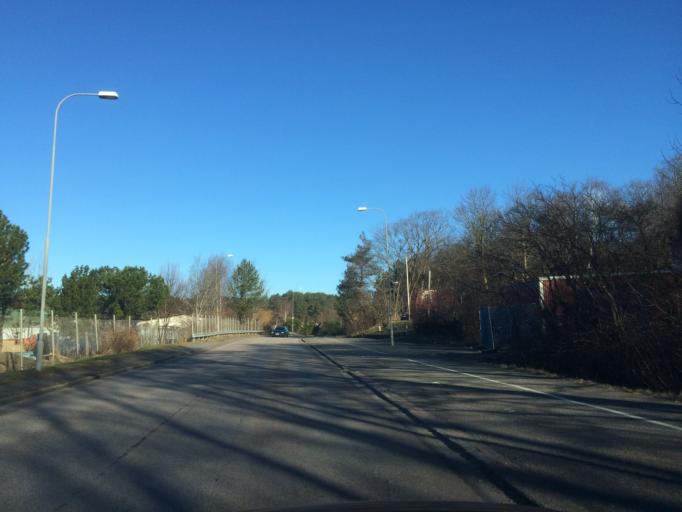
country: SE
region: Vaestra Goetaland
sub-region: Goteborg
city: Majorna
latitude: 57.6624
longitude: 11.8979
